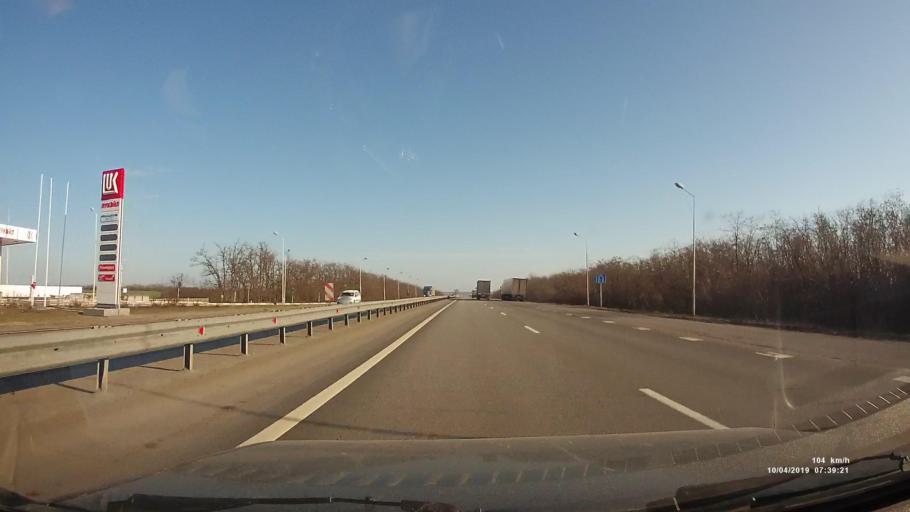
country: RU
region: Rostov
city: Likhoy
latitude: 48.1023
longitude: 40.2591
